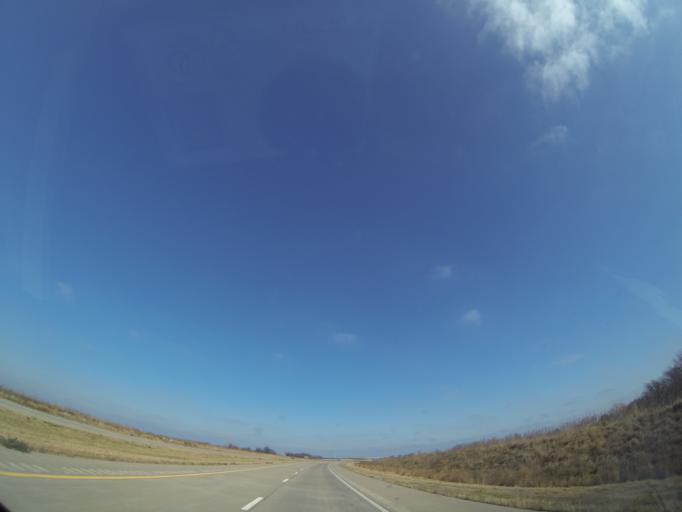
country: US
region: Kansas
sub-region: McPherson County
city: Inman
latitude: 38.2393
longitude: -97.7805
